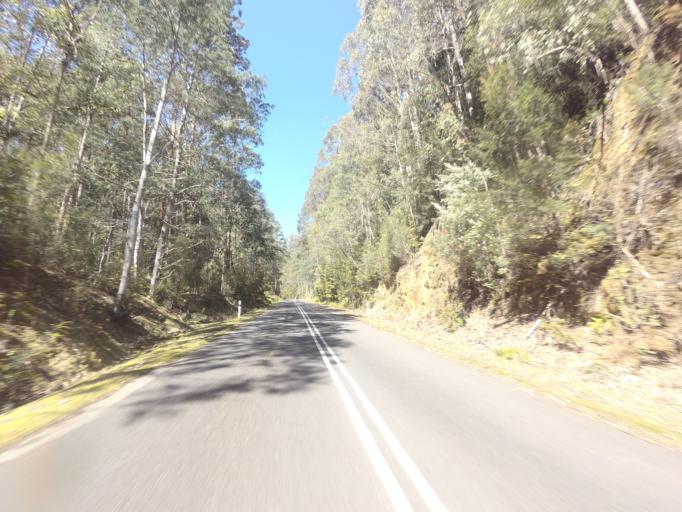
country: AU
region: Tasmania
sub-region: Huon Valley
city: Geeveston
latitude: -42.8259
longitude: 146.3255
